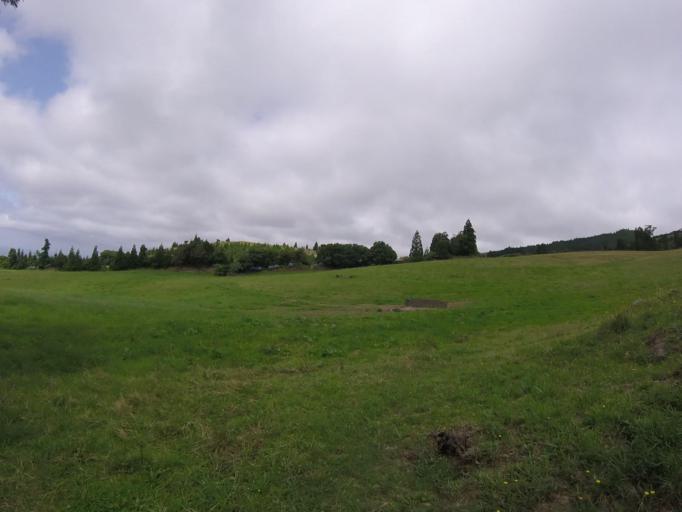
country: PT
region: Azores
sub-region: Vila Franca do Campo
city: Vila Franca do Campo
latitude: 37.7466
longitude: -25.5107
